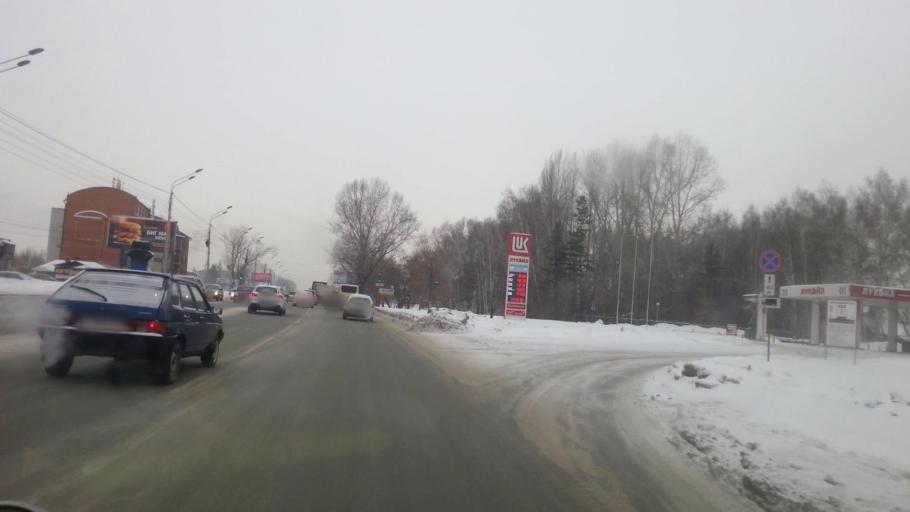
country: RU
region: Altai Krai
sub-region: Gorod Barnaulskiy
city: Barnaul
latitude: 53.3403
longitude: 83.7260
